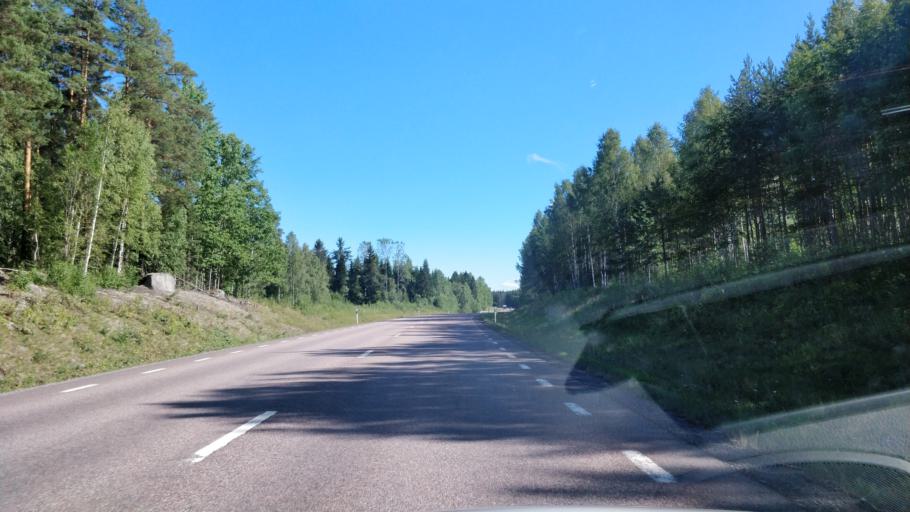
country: SE
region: Dalarna
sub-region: Faluns Kommun
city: Grycksbo
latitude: 60.6590
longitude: 15.5516
